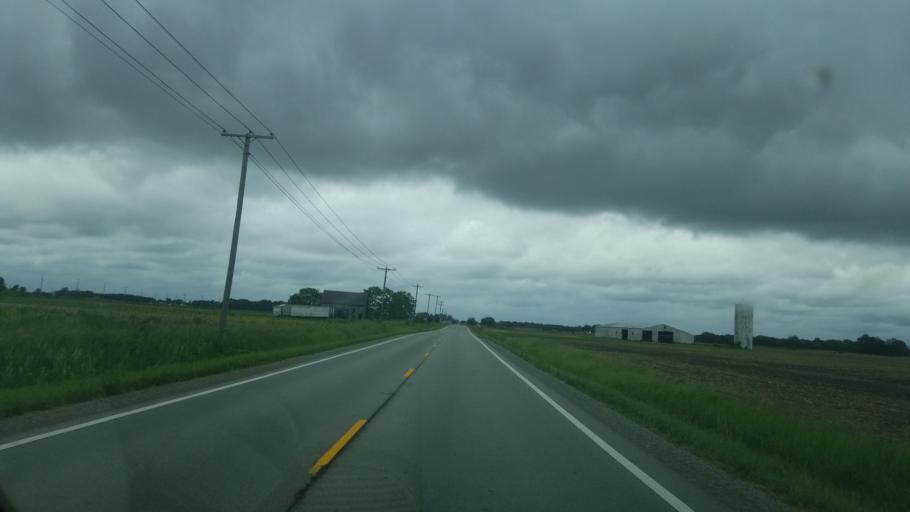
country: US
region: Ohio
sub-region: Marion County
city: Prospect
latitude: 40.4730
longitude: -83.0721
